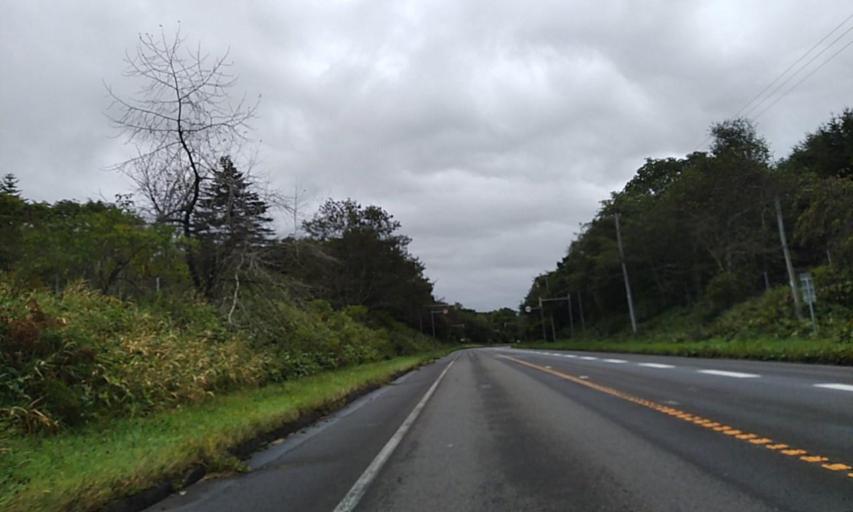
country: JP
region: Hokkaido
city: Kushiro
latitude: 42.9313
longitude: 144.0147
